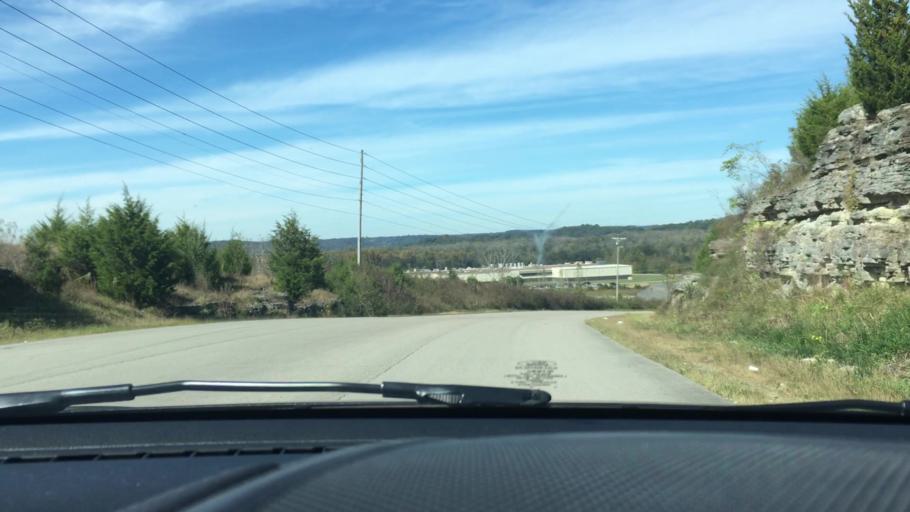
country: US
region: Tennessee
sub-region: Giles County
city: Pulaski
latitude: 35.2240
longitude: -87.0675
